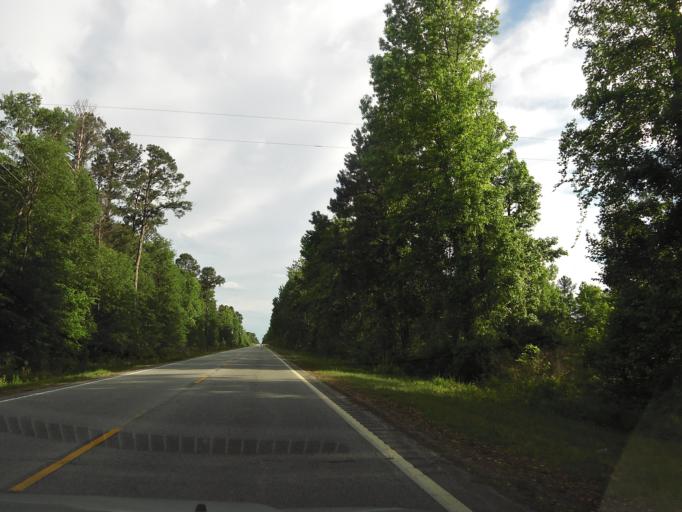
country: US
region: South Carolina
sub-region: Hampton County
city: Estill
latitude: 32.7195
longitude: -81.2422
